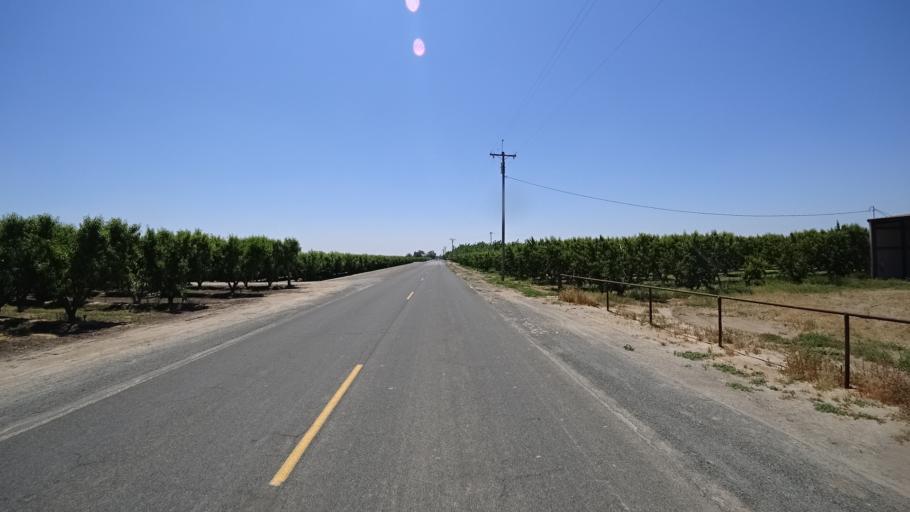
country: US
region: California
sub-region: Fresno County
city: Kingsburg
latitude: 36.4548
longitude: -119.6003
